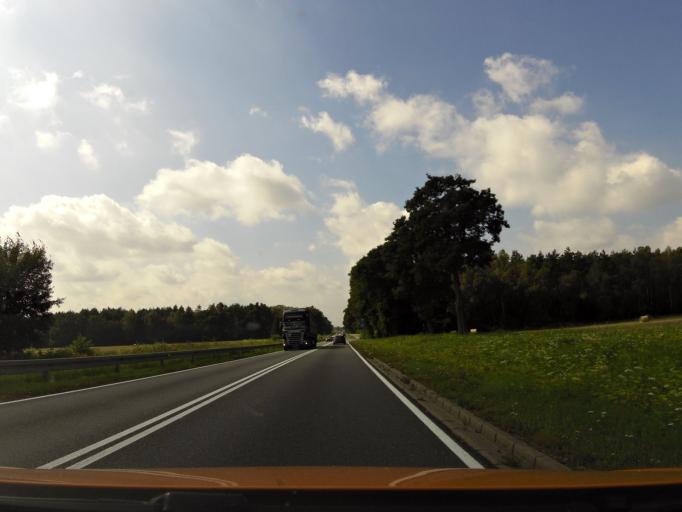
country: PL
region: West Pomeranian Voivodeship
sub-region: Powiat goleniowski
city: Nowogard
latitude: 53.7002
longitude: 15.1668
